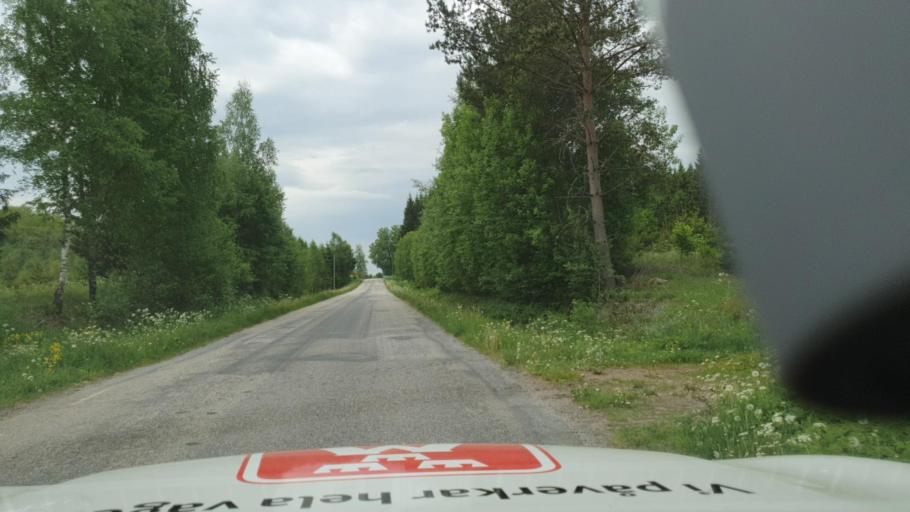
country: SE
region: Vaestra Goetaland
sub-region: Ulricehamns Kommun
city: Ulricehamn
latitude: 57.9432
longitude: 13.3853
